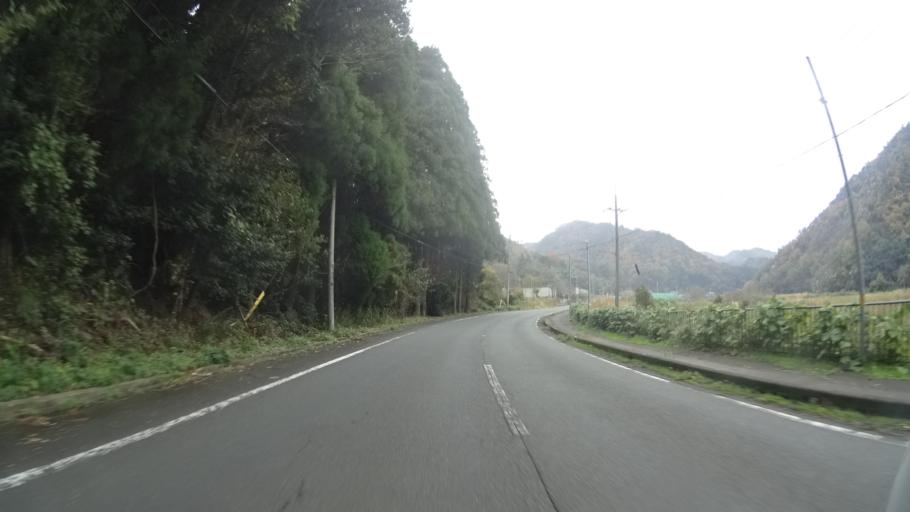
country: JP
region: Kyoto
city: Maizuru
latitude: 35.5051
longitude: 135.4349
